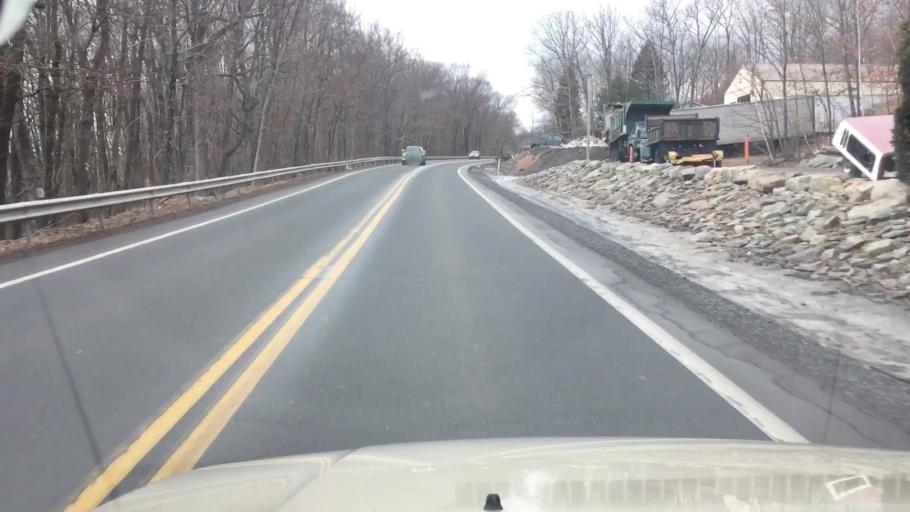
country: US
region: Pennsylvania
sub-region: Luzerne County
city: Harleigh
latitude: 40.9852
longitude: -75.9577
